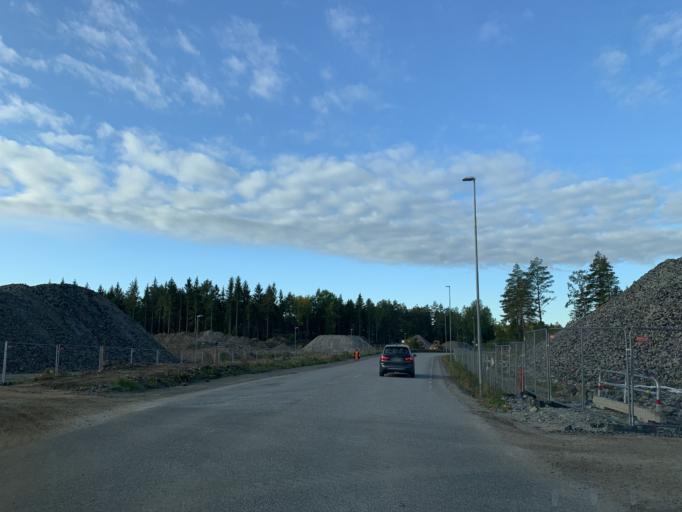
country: SE
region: Stockholm
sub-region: Upplands-Bro Kommun
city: Bro
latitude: 59.5055
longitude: 17.6143
